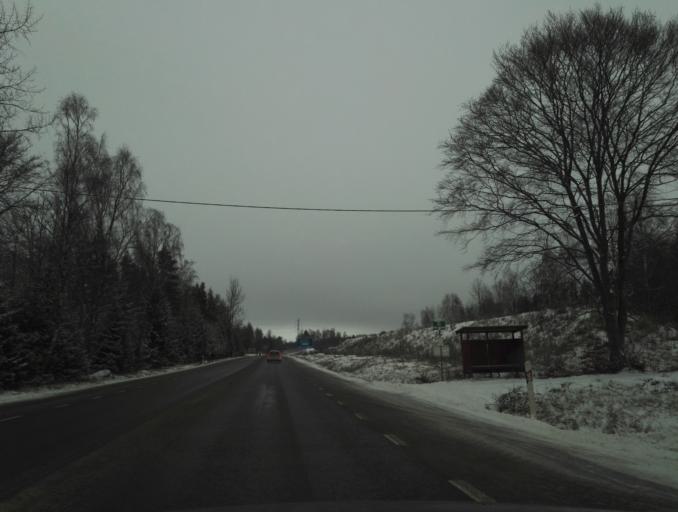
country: SE
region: Kronoberg
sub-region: Vaxjo Kommun
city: Vaexjoe
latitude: 56.8731
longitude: 14.7415
